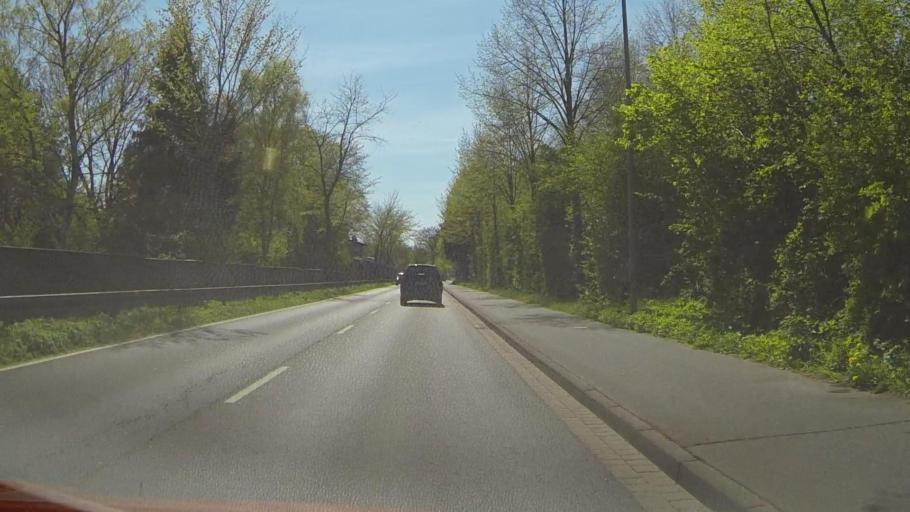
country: DE
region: Schleswig-Holstein
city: Tornesch
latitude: 53.6936
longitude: 9.7036
